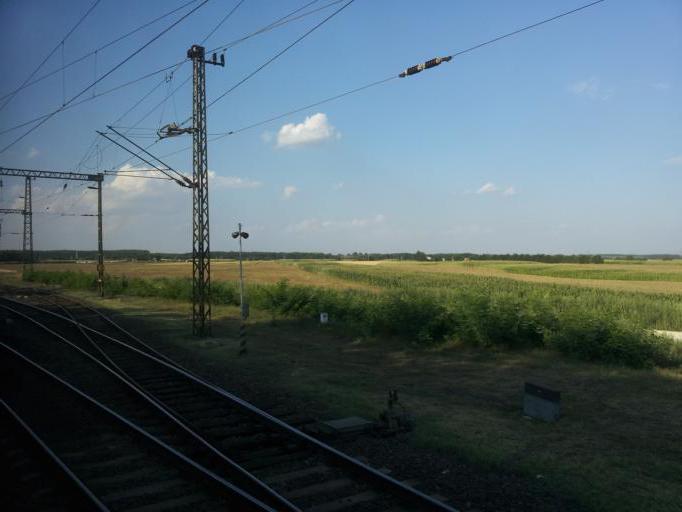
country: HU
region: Pest
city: Taksony
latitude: 47.3167
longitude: 19.0760
